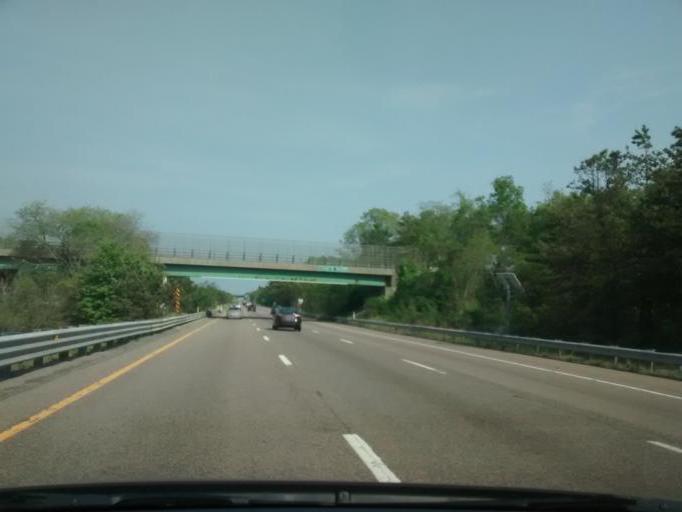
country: US
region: Massachusetts
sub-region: Plymouth County
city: Wareham Center
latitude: 41.7801
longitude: -70.7207
